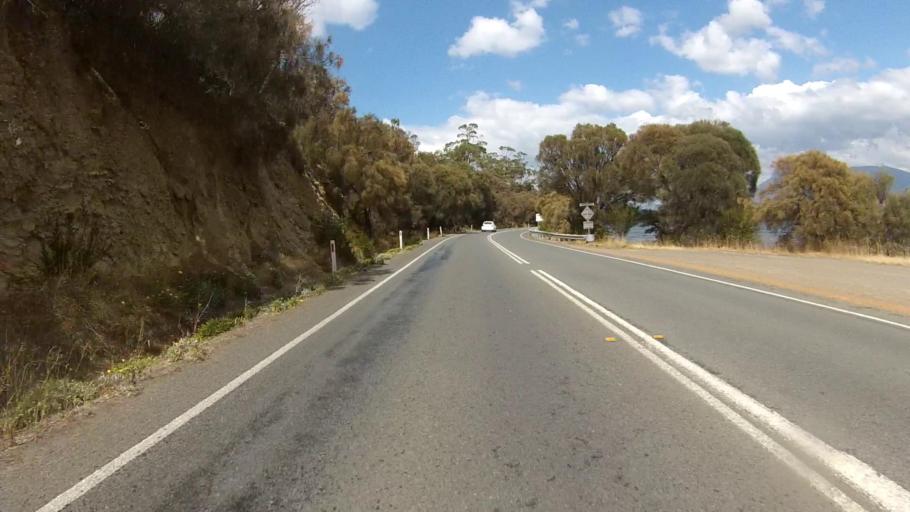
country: AU
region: Tasmania
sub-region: Brighton
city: Old Beach
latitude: -42.7788
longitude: 147.2850
